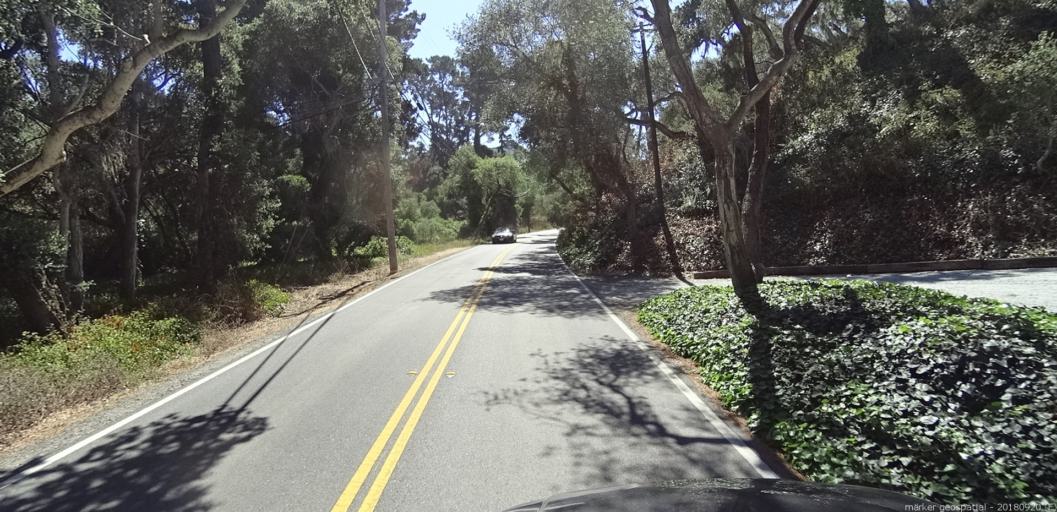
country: US
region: California
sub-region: Monterey County
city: Monterey
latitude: 36.5915
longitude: -121.8701
